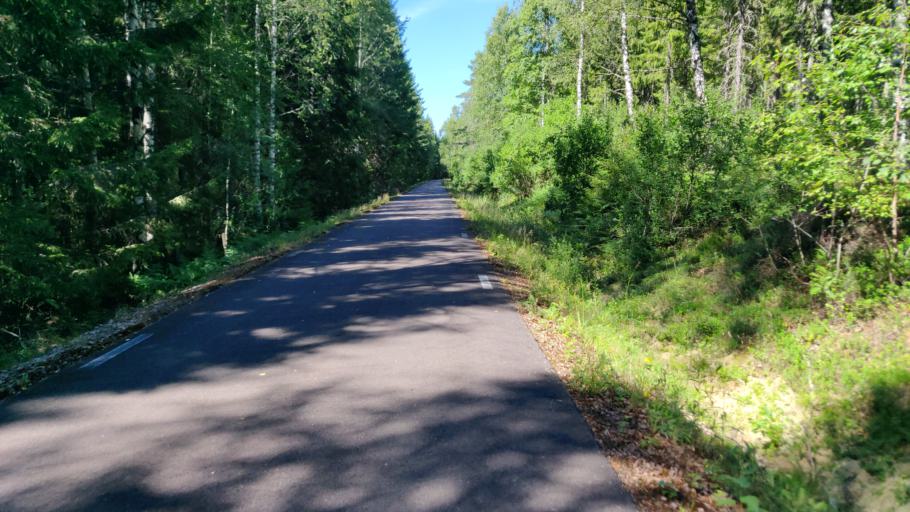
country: SE
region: Vaermland
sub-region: Munkfors Kommun
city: Munkfors
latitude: 59.9481
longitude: 13.5807
